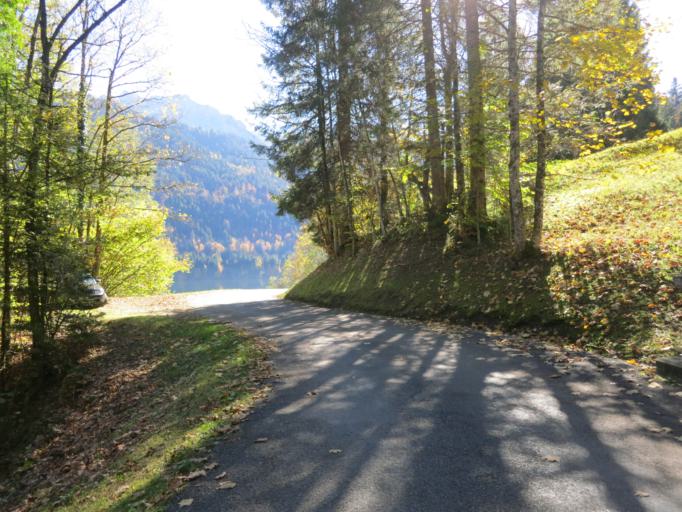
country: CH
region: Schwyz
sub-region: Bezirk March
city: Vorderthal
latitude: 47.0773
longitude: 8.9125
